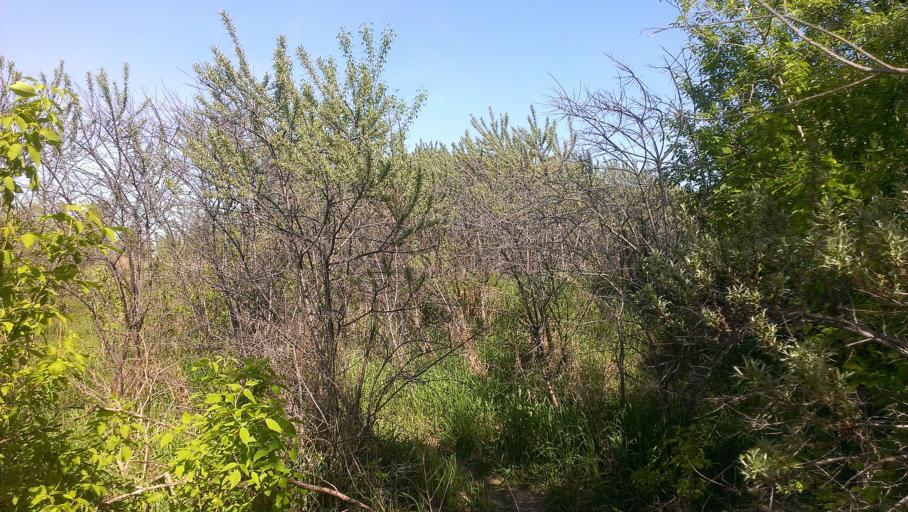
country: RU
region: Altai Krai
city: Sannikovo
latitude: 53.3200
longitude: 83.9455
